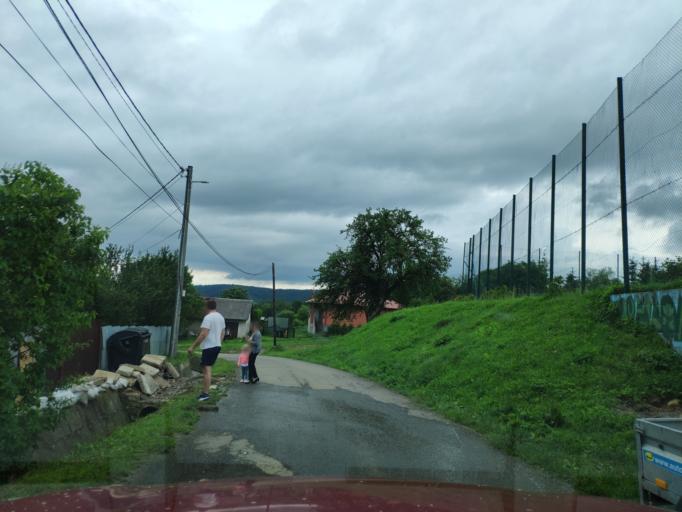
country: SK
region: Presovsky
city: Sabinov
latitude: 49.0433
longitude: 21.0150
